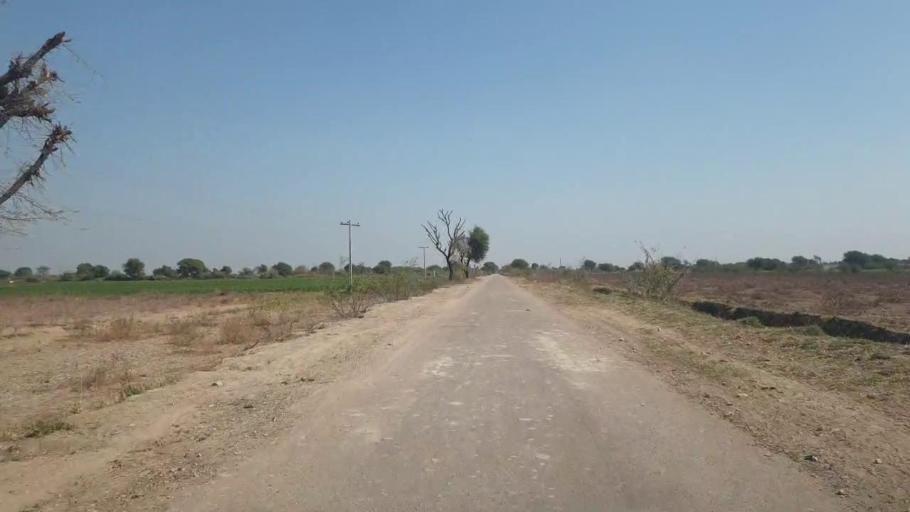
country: PK
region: Sindh
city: Chambar
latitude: 25.2887
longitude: 68.6699
